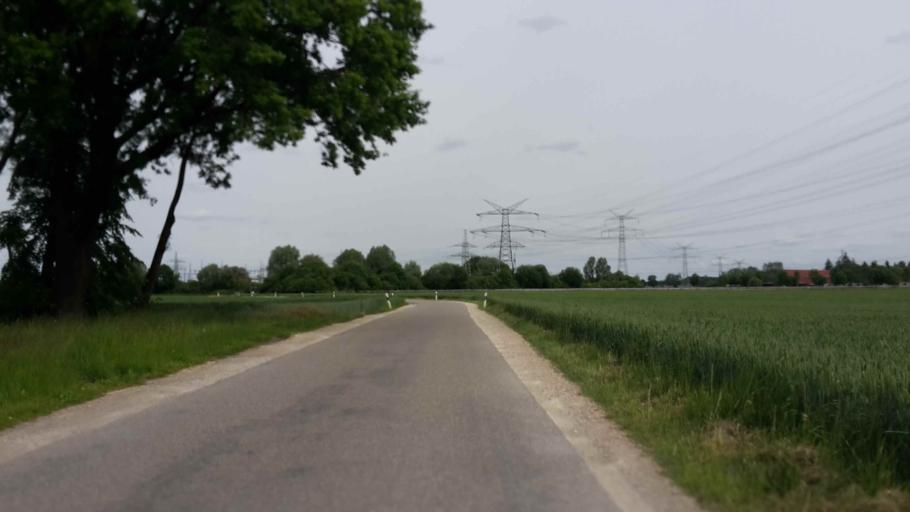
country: DE
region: Bavaria
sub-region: Upper Bavaria
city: Karlsfeld
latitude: 48.2179
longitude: 11.4293
